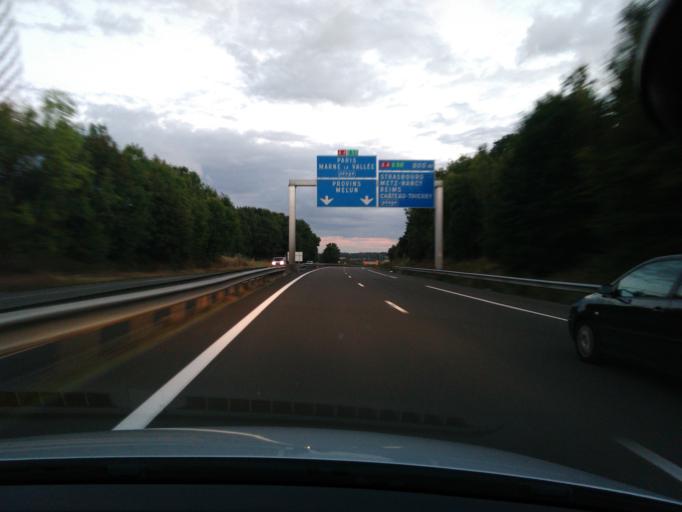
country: FR
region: Ile-de-France
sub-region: Departement de Seine-et-Marne
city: Quincy-Voisins
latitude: 48.8960
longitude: 2.8939
